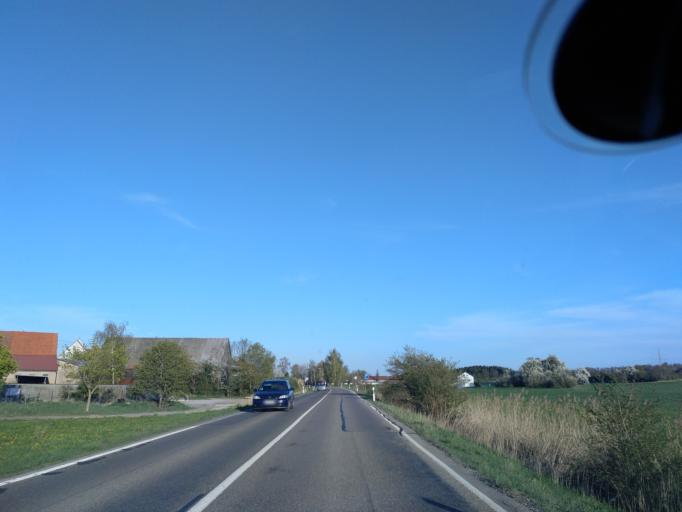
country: DE
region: Baden-Wuerttemberg
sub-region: Regierungsbezirk Stuttgart
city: Kirchberg an der Jagst
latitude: 49.1420
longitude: 9.9931
